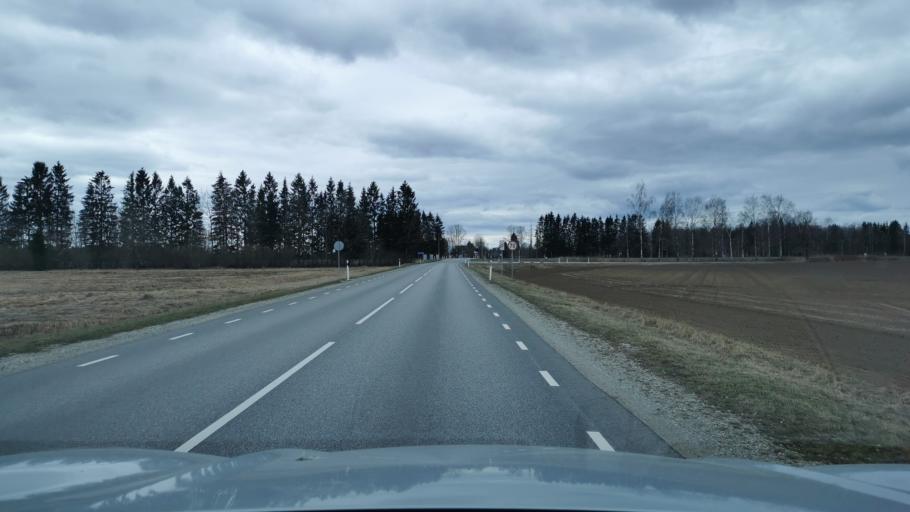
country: EE
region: Ida-Virumaa
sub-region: Puessi linn
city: Pussi
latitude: 59.3588
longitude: 27.0241
